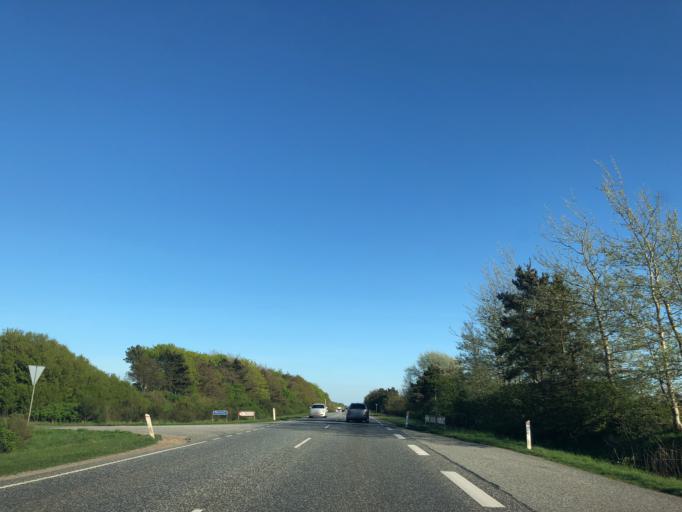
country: DK
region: Central Jutland
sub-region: Herning Kommune
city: Avlum
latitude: 56.3001
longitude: 8.7156
